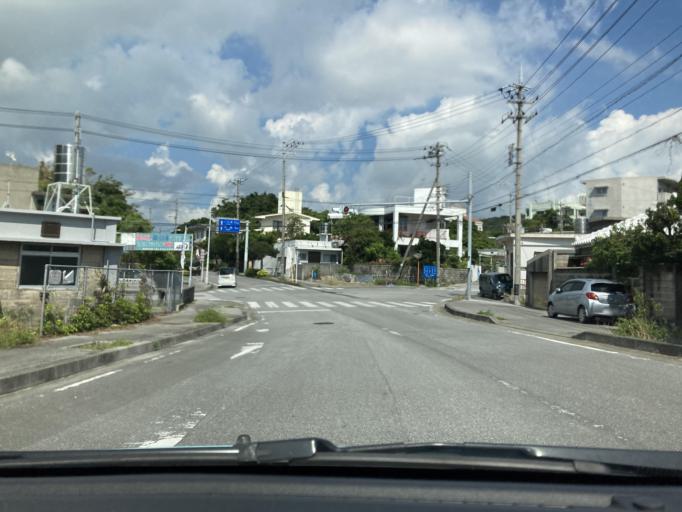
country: JP
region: Okinawa
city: Tomigusuku
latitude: 26.1424
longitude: 127.7684
